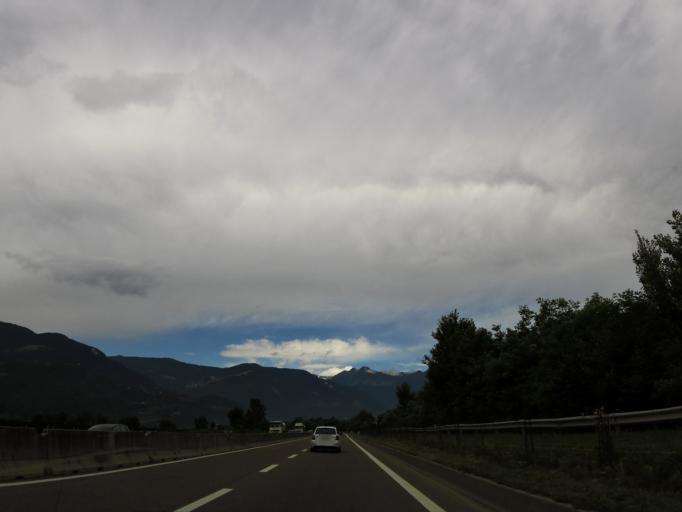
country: IT
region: Trentino-Alto Adige
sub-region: Bolzano
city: Nalles
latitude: 46.5650
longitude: 11.2134
